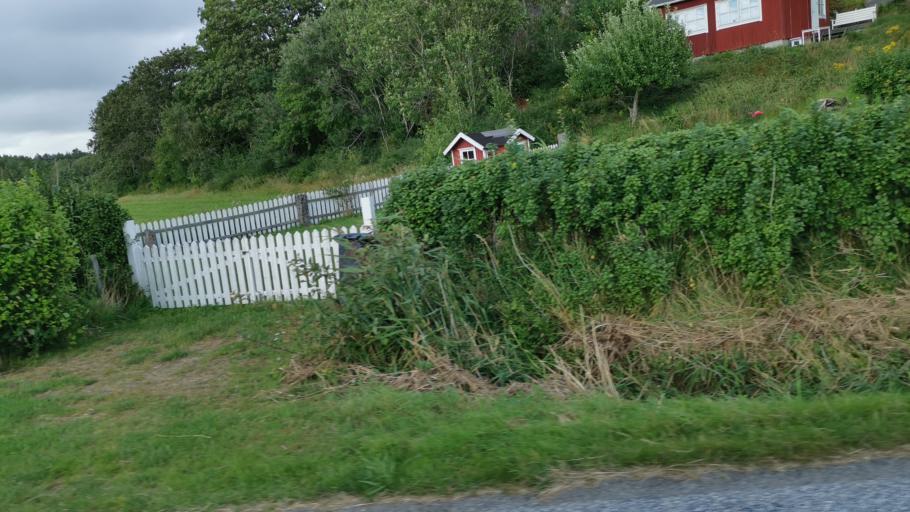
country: SE
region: Vaestra Goetaland
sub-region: Sotenas Kommun
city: Hunnebostrand
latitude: 58.5233
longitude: 11.2983
